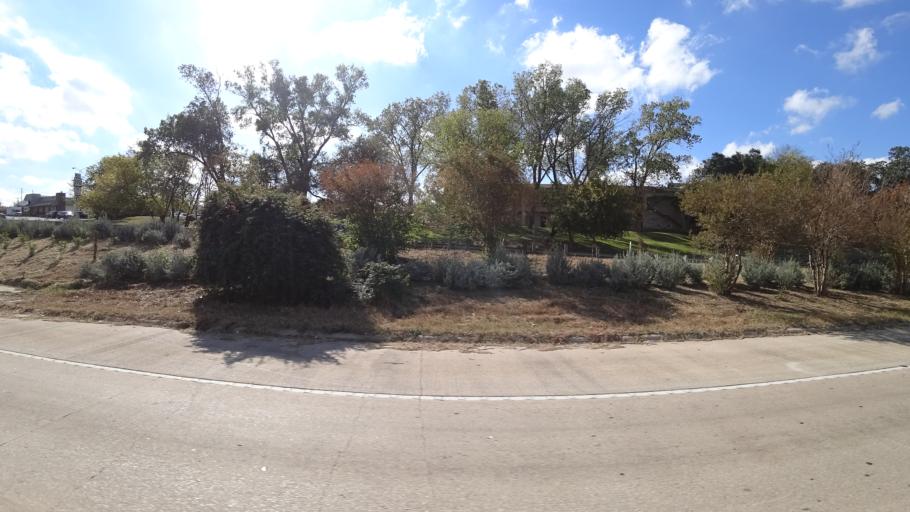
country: US
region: Texas
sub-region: Travis County
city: Austin
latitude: 30.2274
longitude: -97.7719
